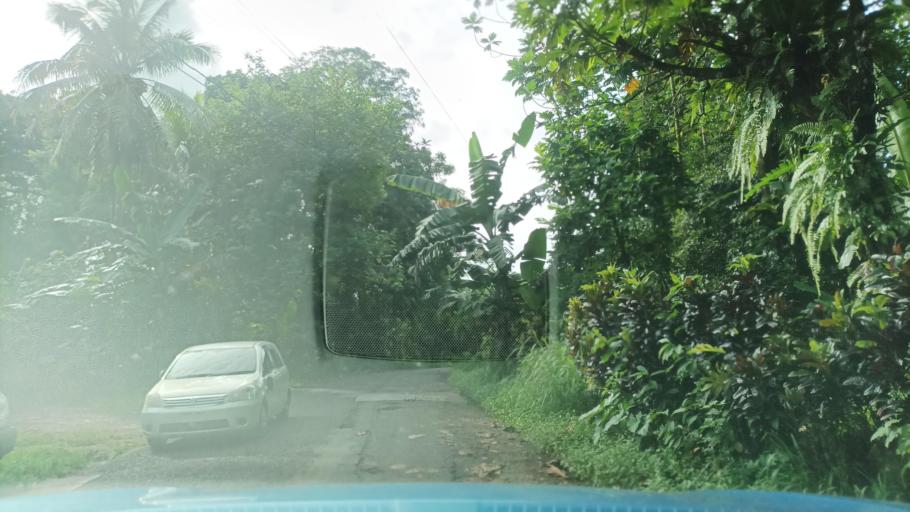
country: FM
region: Pohnpei
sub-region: Kolonia Municipality
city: Kolonia
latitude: 6.9526
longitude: 158.2259
